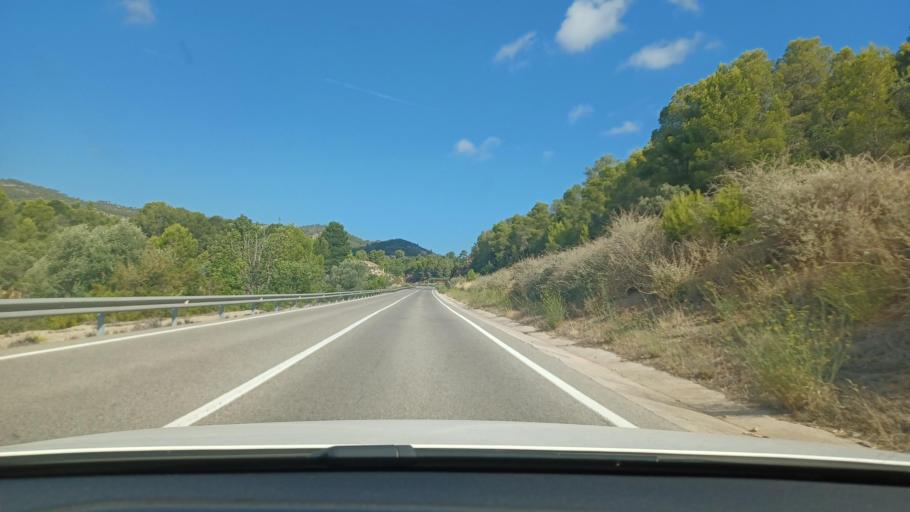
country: ES
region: Catalonia
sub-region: Provincia de Tarragona
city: Tivenys
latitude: 40.9380
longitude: 0.4680
